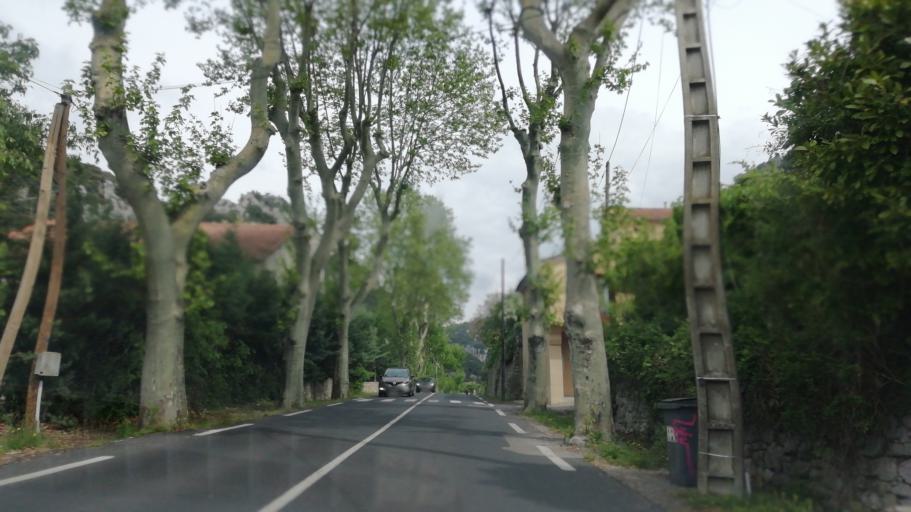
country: FR
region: Languedoc-Roussillon
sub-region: Departement de l'Herault
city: Saint-Bauzille-de-Putois
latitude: 43.9047
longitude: 3.7379
